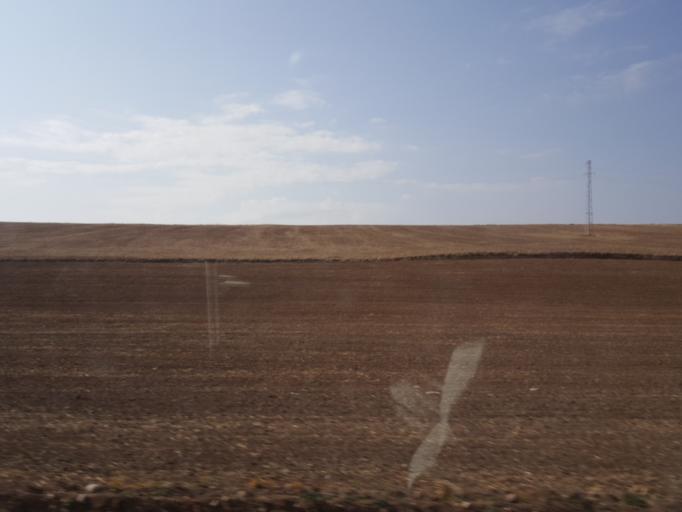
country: TR
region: Corum
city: Cemilbey
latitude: 40.1749
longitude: 35.0392
